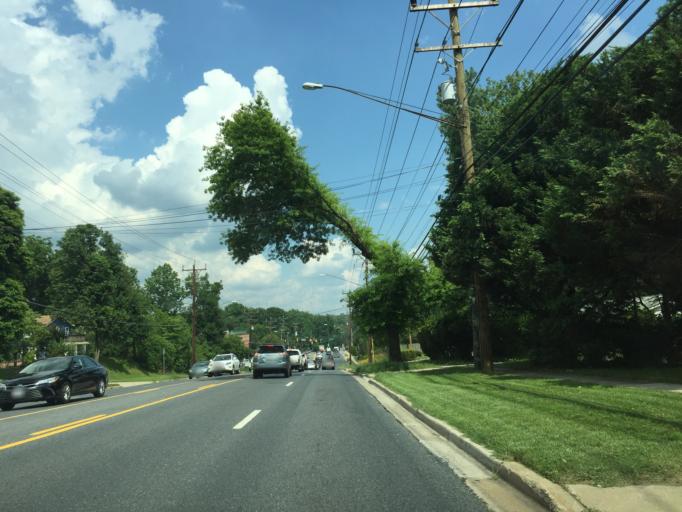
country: US
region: Maryland
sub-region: Montgomery County
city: North Bethesda
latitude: 39.0538
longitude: -77.0974
